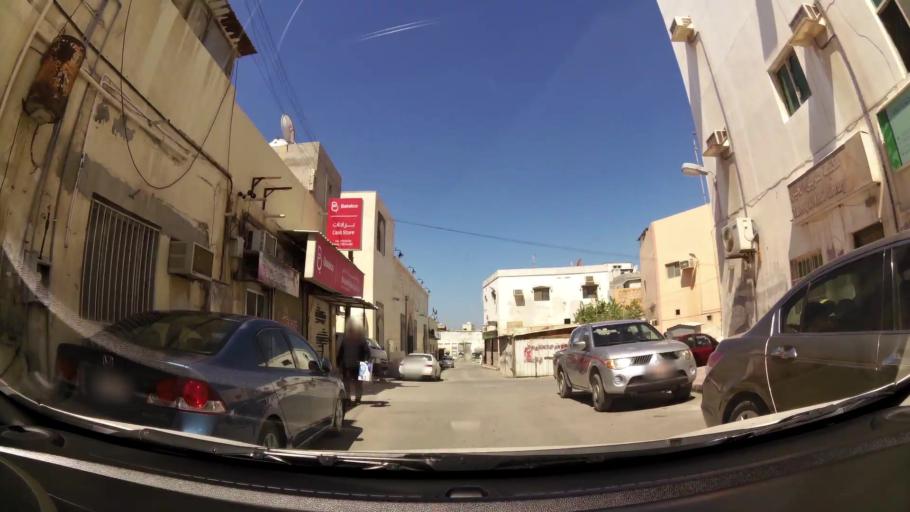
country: BH
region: Muharraq
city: Al Muharraq
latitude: 26.2845
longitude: 50.6239
